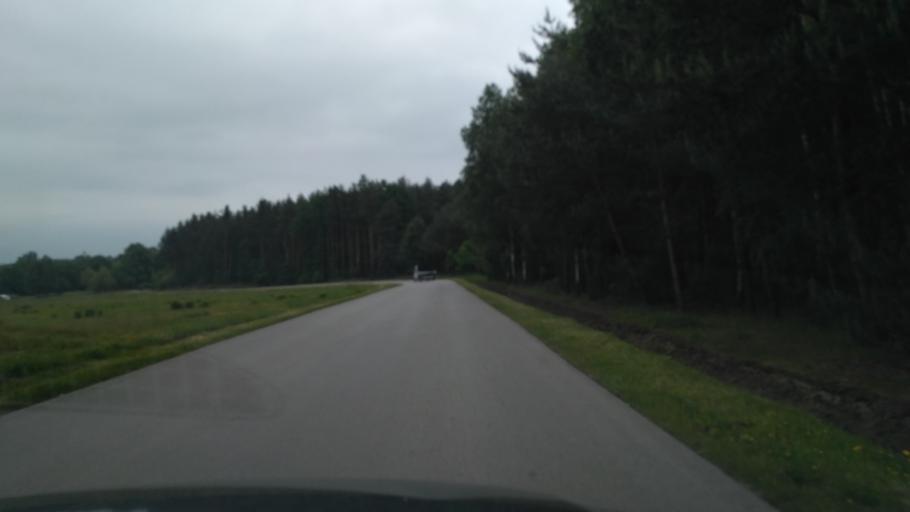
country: PL
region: Subcarpathian Voivodeship
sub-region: Powiat kolbuszowski
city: Niwiska
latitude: 50.2144
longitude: 21.6353
